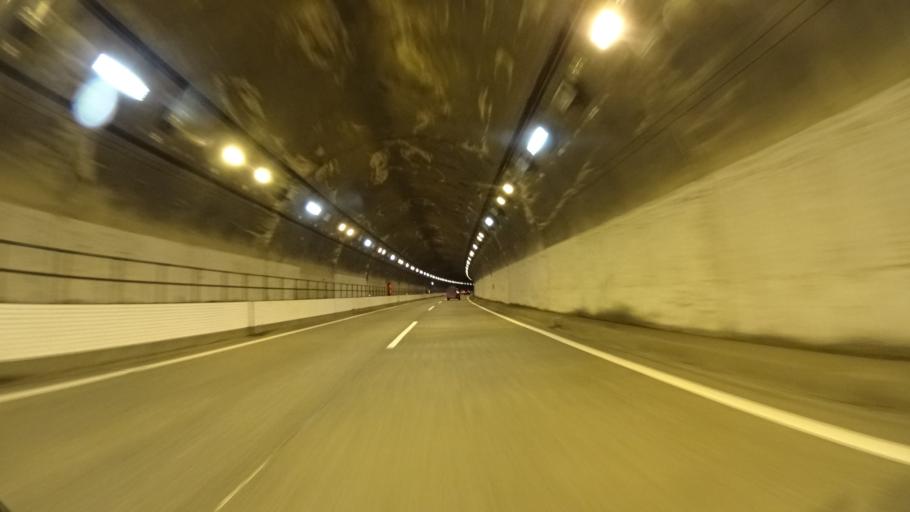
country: JP
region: Nagano
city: Nagano-shi
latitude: 36.5608
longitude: 138.1685
